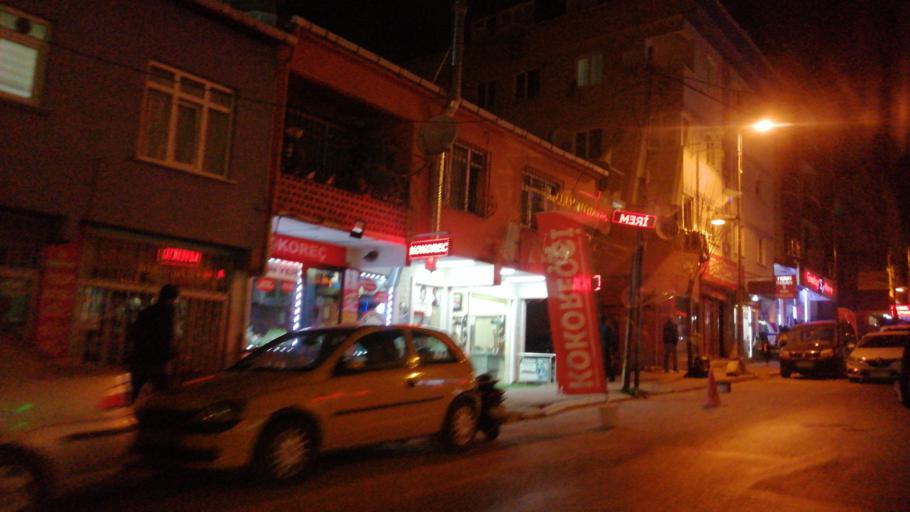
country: TR
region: Istanbul
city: Umraniye
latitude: 41.0127
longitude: 29.1282
